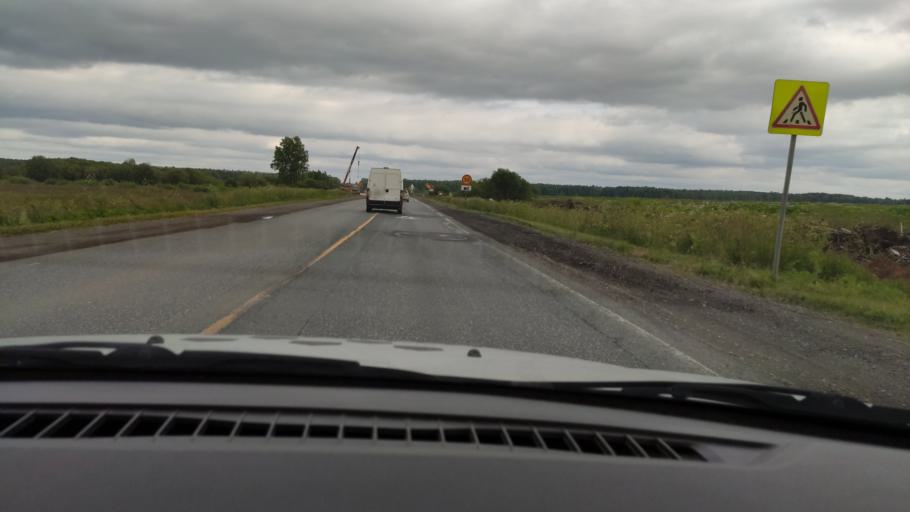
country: RU
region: Perm
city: Kukushtan
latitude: 57.6126
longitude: 56.4977
